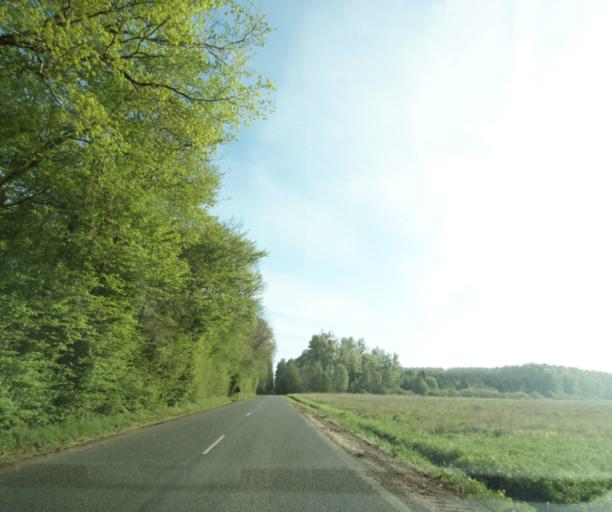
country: FR
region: Ile-de-France
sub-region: Departement de Seine-et-Marne
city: Vernou-la-Celle-sur-Seine
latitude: 48.4092
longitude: 2.8379
